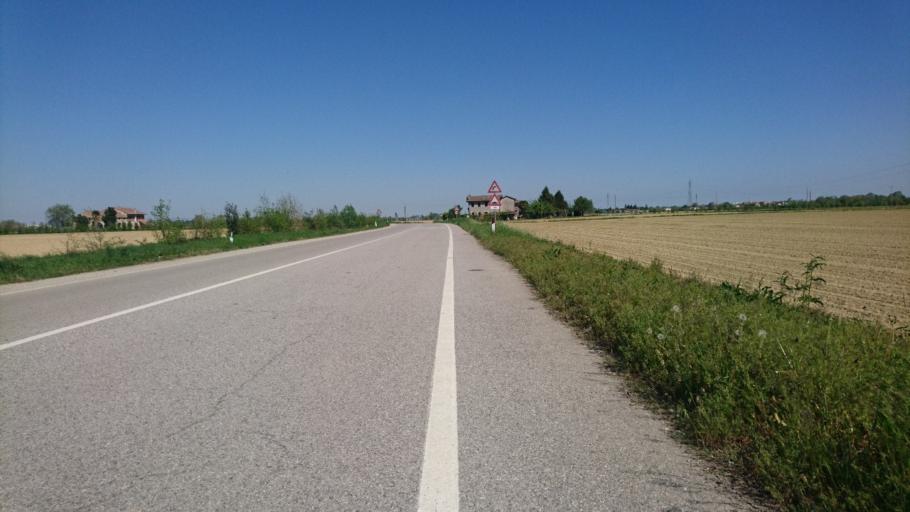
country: IT
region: Veneto
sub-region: Provincia di Venezia
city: Marcon-Gaggio-Colmello
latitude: 45.5736
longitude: 12.2849
